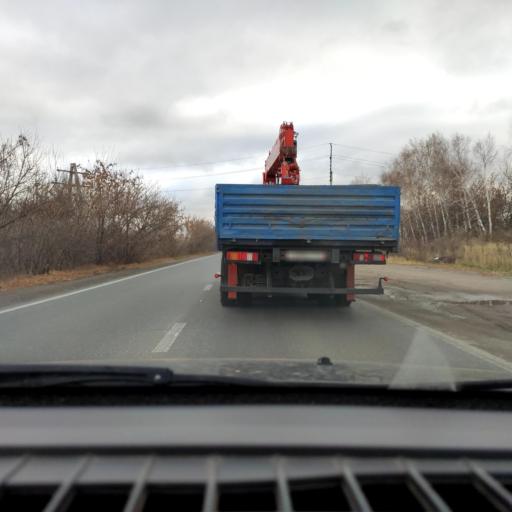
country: RU
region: Samara
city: Tol'yatti
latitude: 53.5590
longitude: 49.3603
